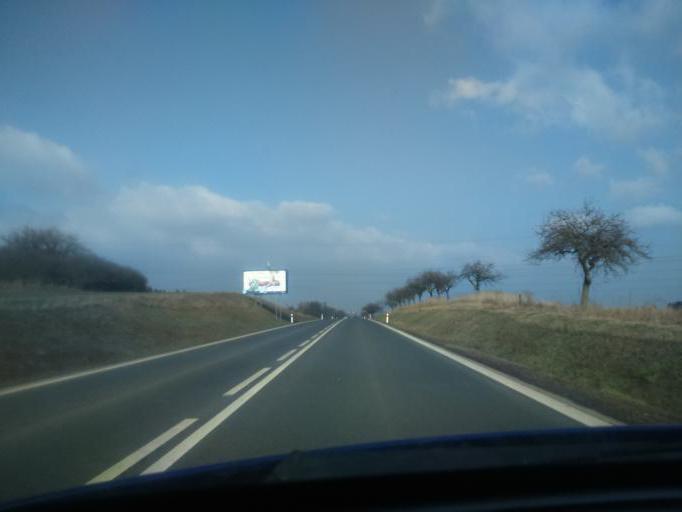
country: CZ
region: Plzensky
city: Stod
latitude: 49.6233
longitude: 13.1452
